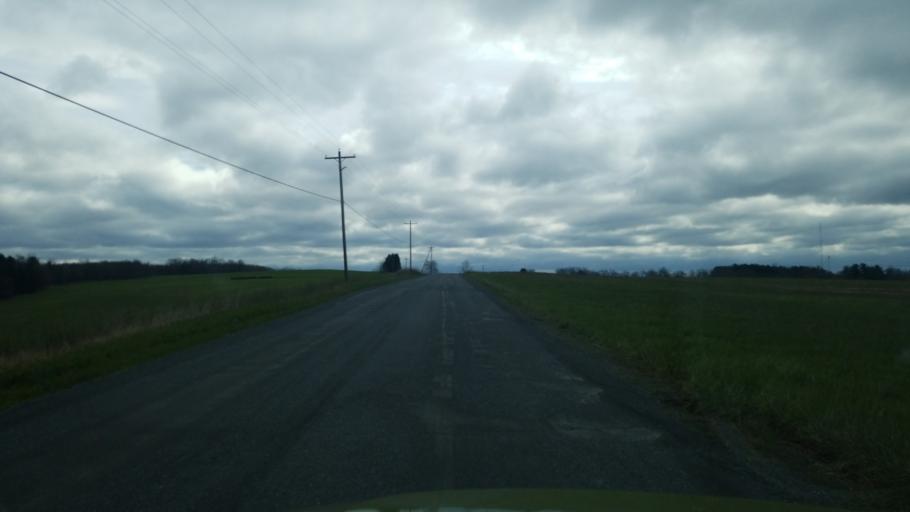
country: US
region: Pennsylvania
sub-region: Clearfield County
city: Clearfield
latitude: 41.0785
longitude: -78.3819
